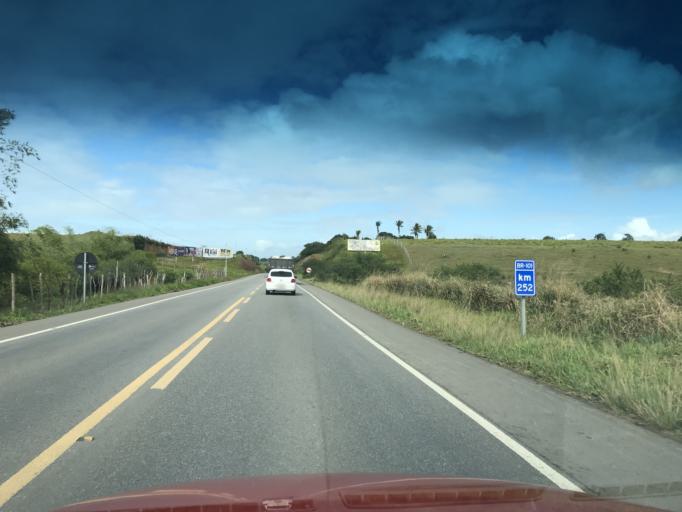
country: BR
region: Bahia
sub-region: Conceicao Do Almeida
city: Muritiba
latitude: -12.8989
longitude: -39.2357
